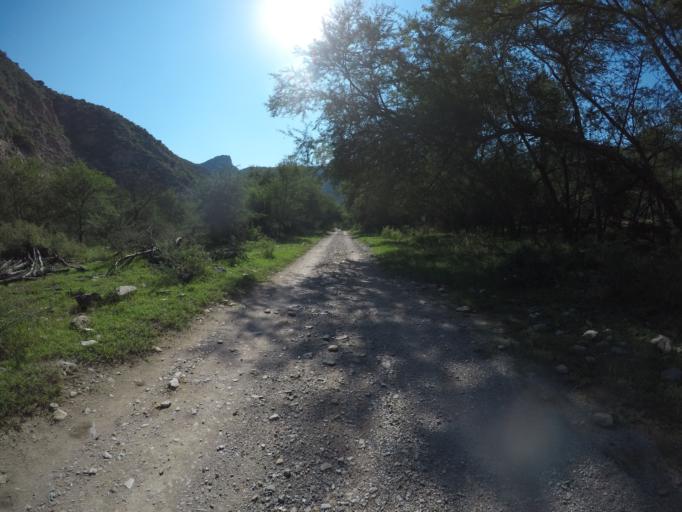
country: ZA
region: Eastern Cape
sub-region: Cacadu District Municipality
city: Kareedouw
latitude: -33.6583
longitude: 24.3662
